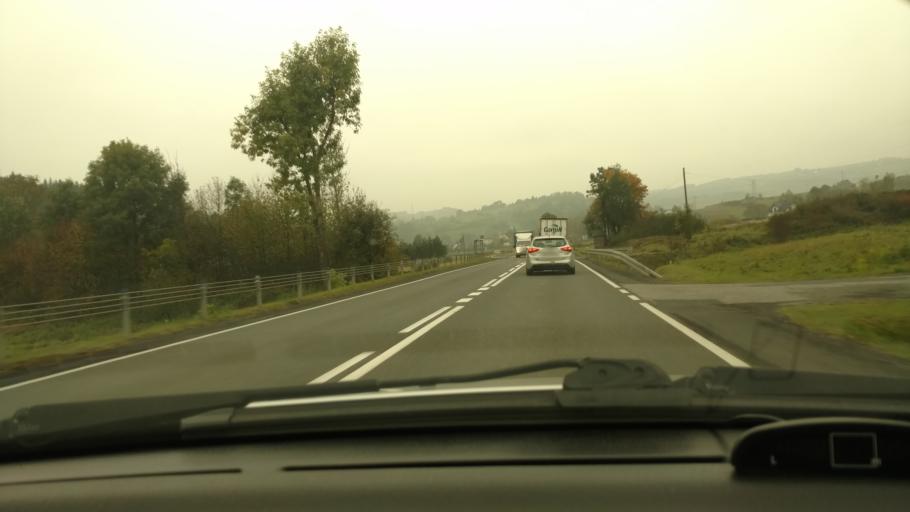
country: PL
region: Lesser Poland Voivodeship
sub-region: Powiat nowosadecki
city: Kamionka Wielka
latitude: 49.6184
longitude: 20.7978
